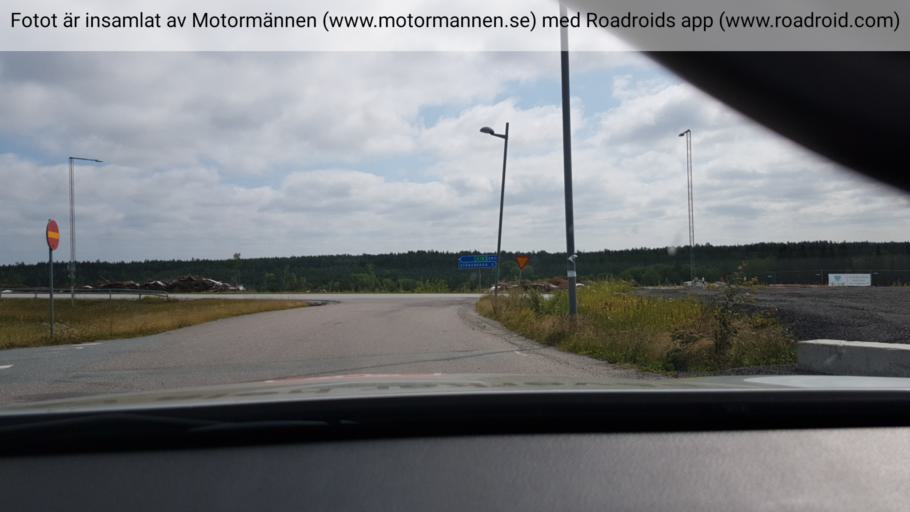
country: SE
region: Stockholm
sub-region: Norrtalje Kommun
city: Rimbo
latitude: 59.6345
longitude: 18.3317
